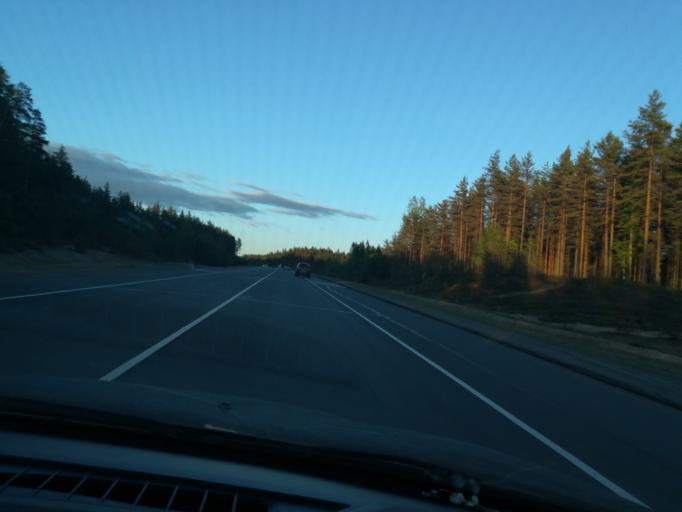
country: RU
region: Leningrad
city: Yakovlevo
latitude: 60.3618
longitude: 29.5670
